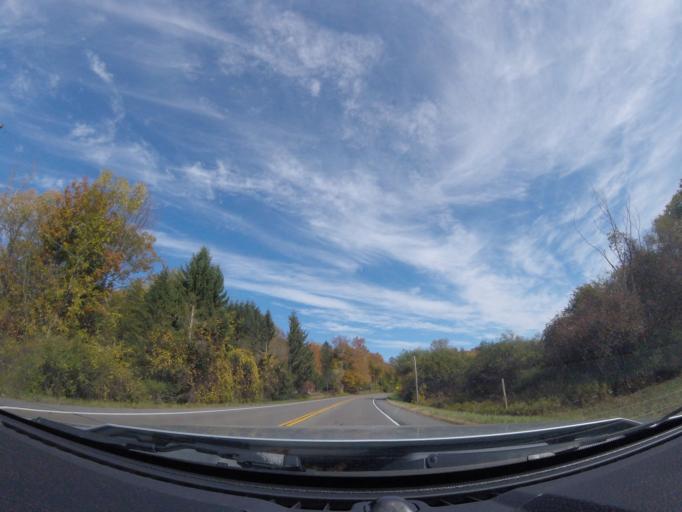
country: US
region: New York
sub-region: Cortland County
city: Cortland West
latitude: 42.5685
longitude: -76.2581
